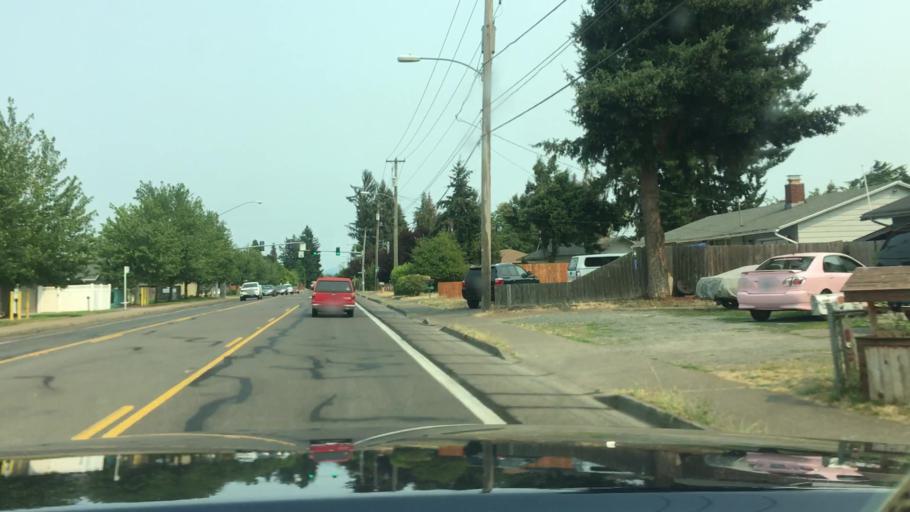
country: US
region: Oregon
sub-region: Lane County
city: Eugene
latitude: 44.0845
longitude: -123.1621
